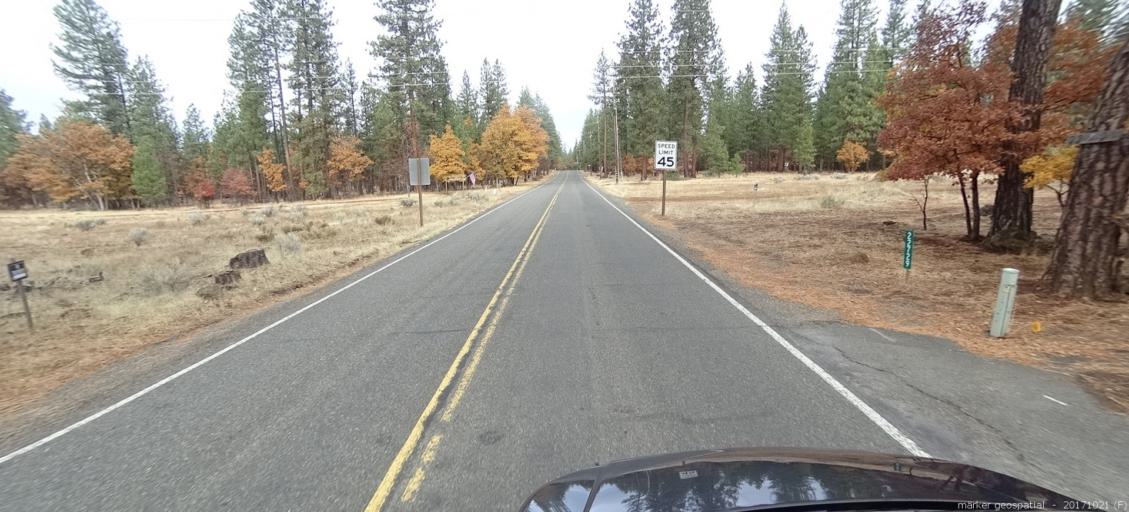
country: US
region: California
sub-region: Shasta County
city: Burney
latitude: 40.9492
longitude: -121.5724
